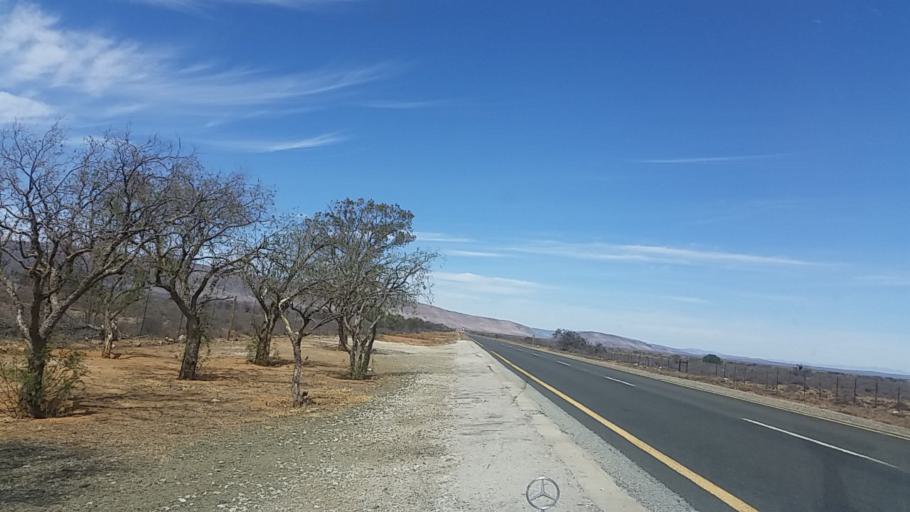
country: ZA
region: Eastern Cape
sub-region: Cacadu District Municipality
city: Willowmore
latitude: -32.9830
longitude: 23.5691
